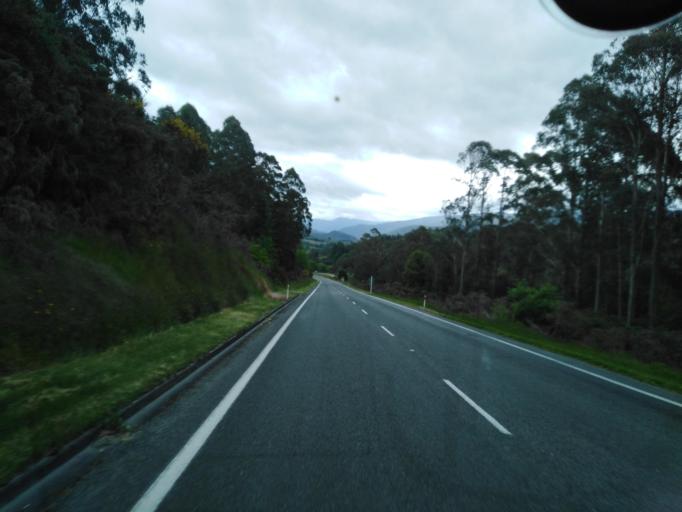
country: NZ
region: Tasman
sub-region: Tasman District
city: Wakefield
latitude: -41.6288
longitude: 172.6983
